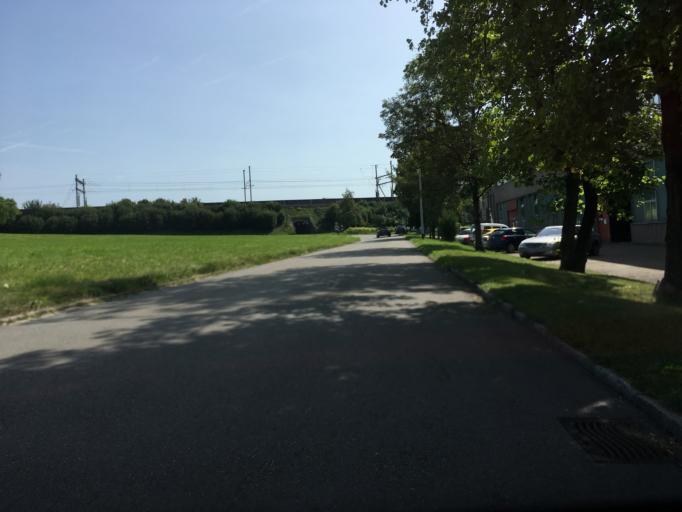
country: CH
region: Zurich
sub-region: Bezirk Buelach
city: Dietlikon / Eichwiesen
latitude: 47.4264
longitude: 8.6229
